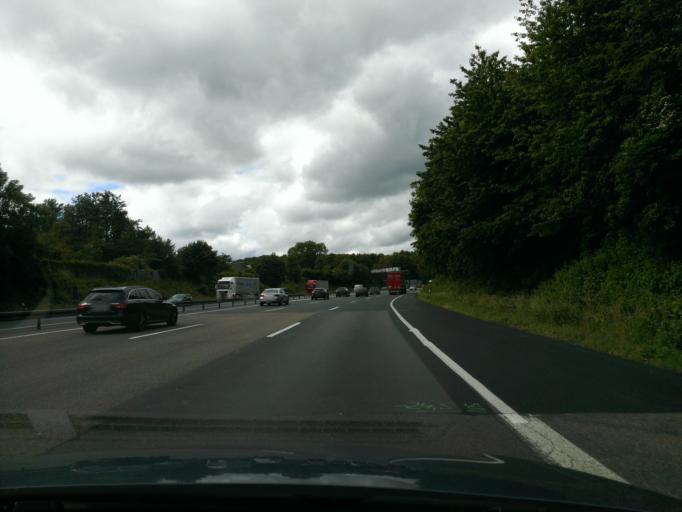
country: DE
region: North Rhine-Westphalia
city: Herdecke
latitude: 51.3810
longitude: 7.4356
